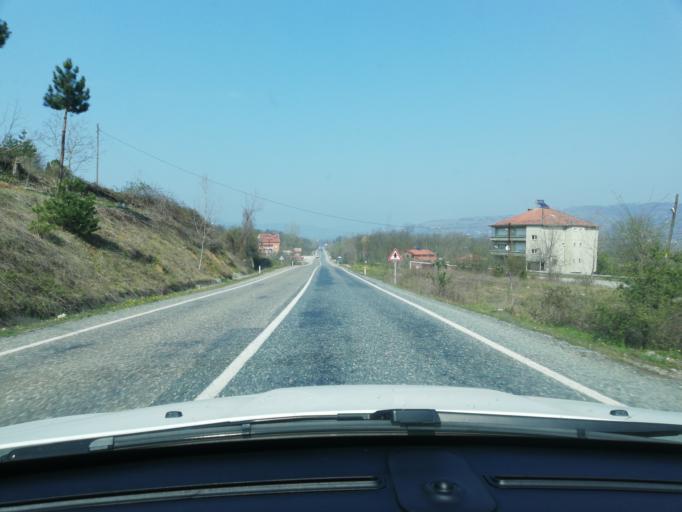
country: TR
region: Zonguldak
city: Gokcebey
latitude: 41.2896
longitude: 32.1393
